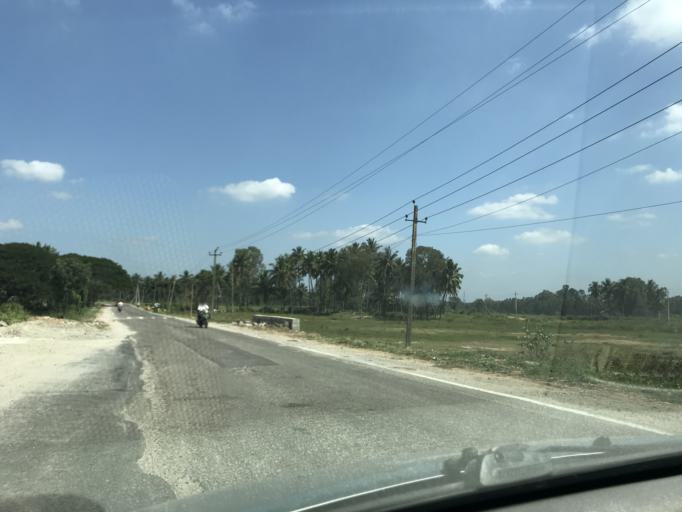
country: IN
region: Karnataka
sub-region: Mysore
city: Hunsur
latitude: 12.3483
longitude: 76.2893
